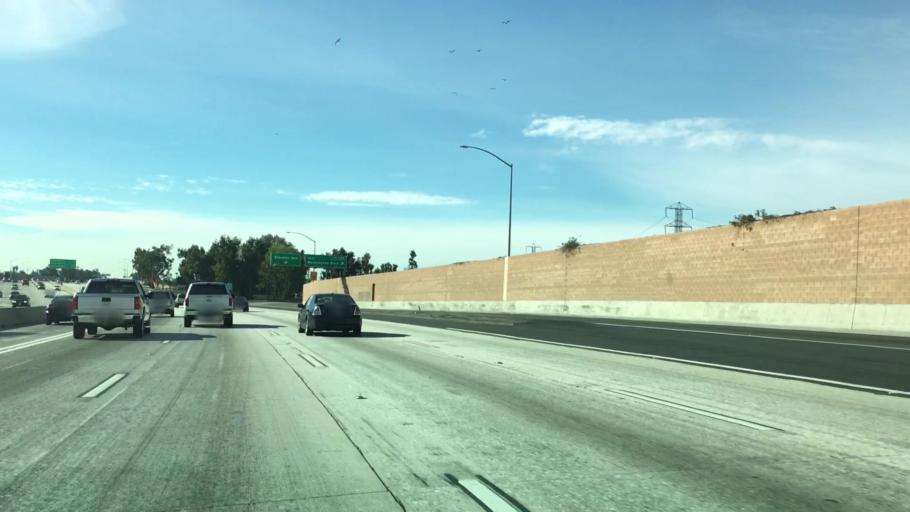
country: US
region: California
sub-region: Los Angeles County
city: West Whittier-Los Nietos
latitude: 33.9777
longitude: -118.0788
